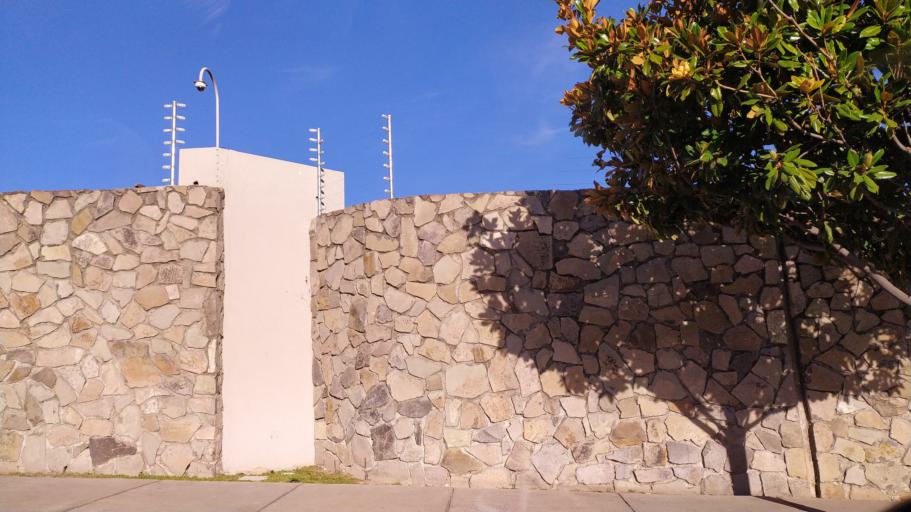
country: MX
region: Jalisco
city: Zapopan2
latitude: 20.6982
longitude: -103.4266
